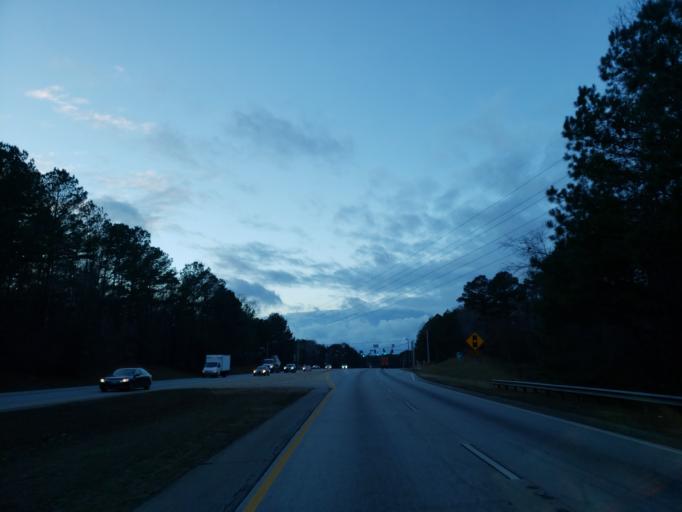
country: US
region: Georgia
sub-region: Fulton County
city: Union City
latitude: 33.6837
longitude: -84.5634
